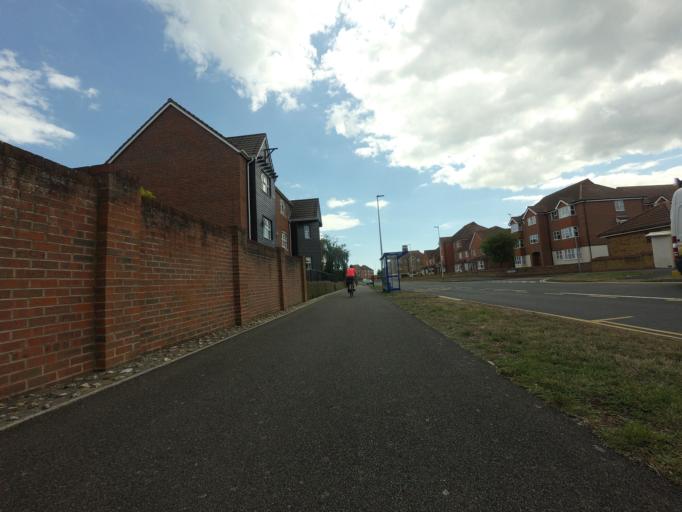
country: GB
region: England
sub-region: East Sussex
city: Pevensey
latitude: 50.7919
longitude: 0.3215
